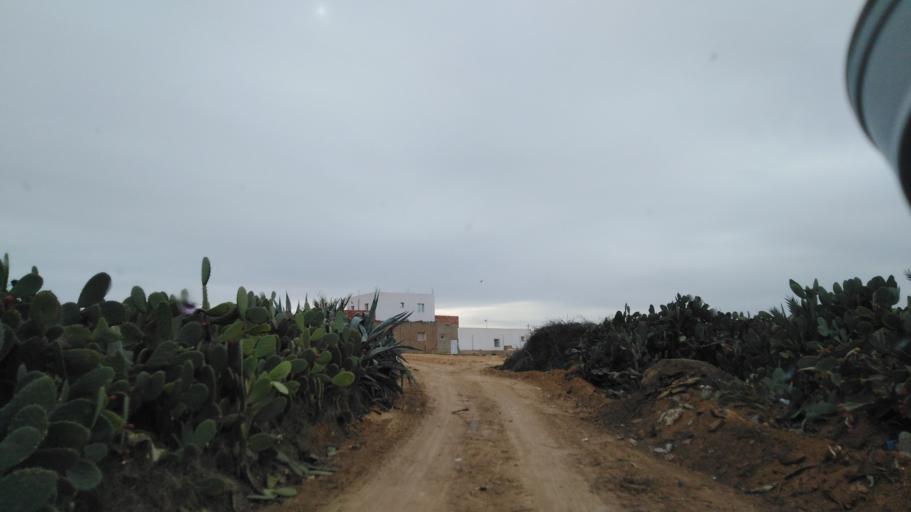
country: TN
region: Safaqis
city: Bi'r `Ali Bin Khalifah
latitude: 34.7658
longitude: 10.3763
